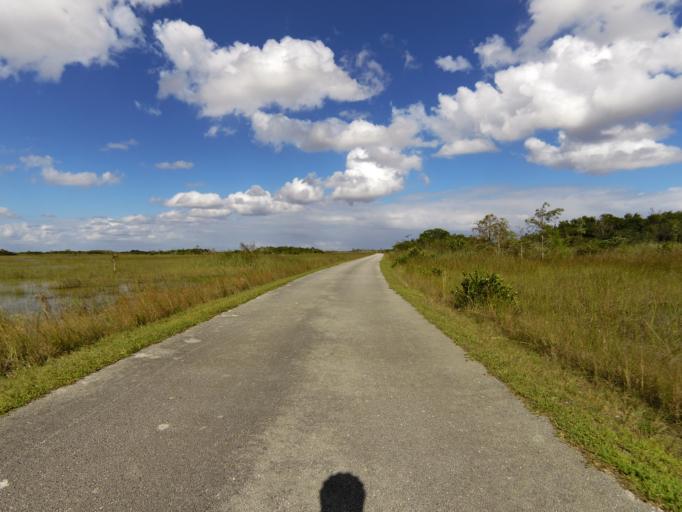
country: US
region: Florida
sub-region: Miami-Dade County
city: The Hammocks
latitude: 25.7126
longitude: -80.7613
